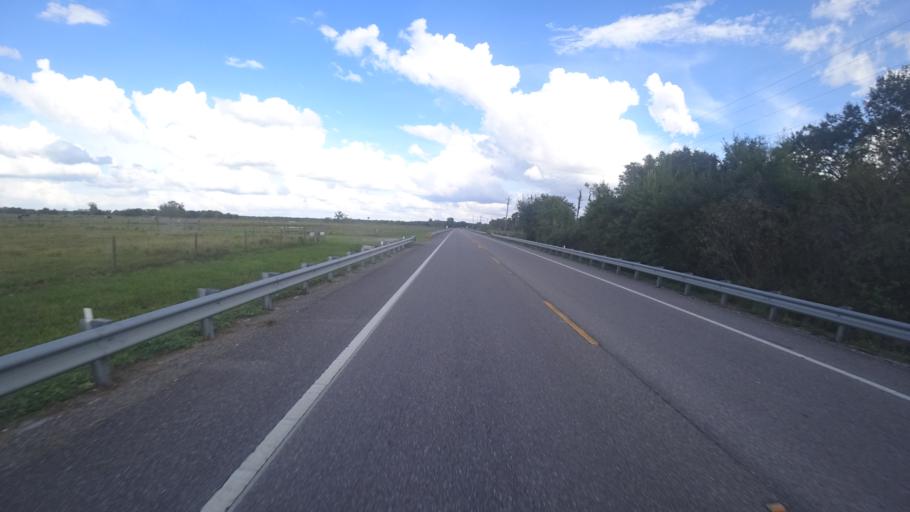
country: US
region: Florida
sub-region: Sarasota County
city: Lake Sarasota
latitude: 27.3868
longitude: -82.2571
